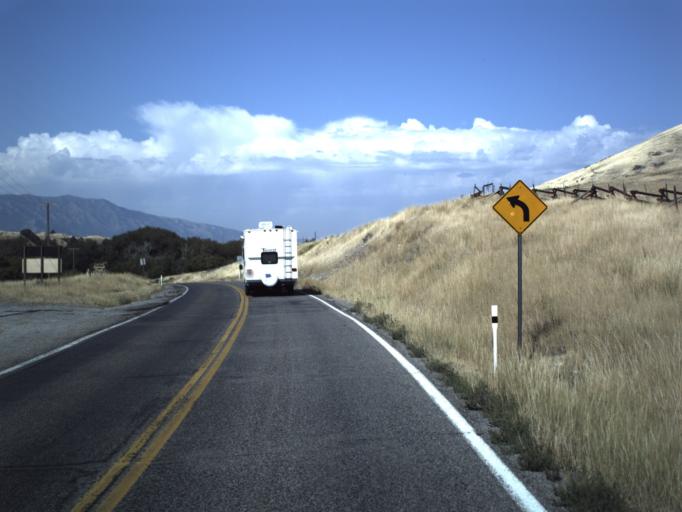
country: US
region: Utah
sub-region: Cache County
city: Hyrum
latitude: 41.6259
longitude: -111.7964
